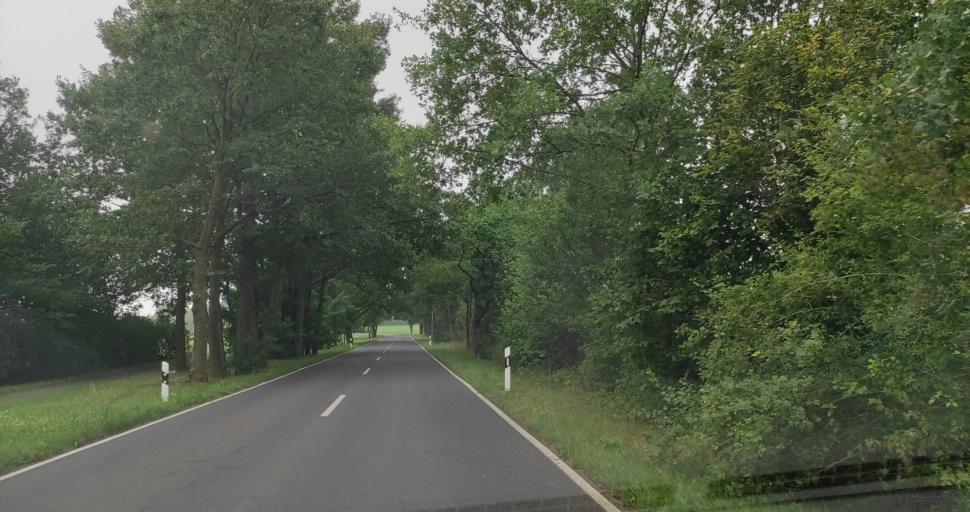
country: DE
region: Brandenburg
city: Forst
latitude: 51.7063
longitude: 14.6260
